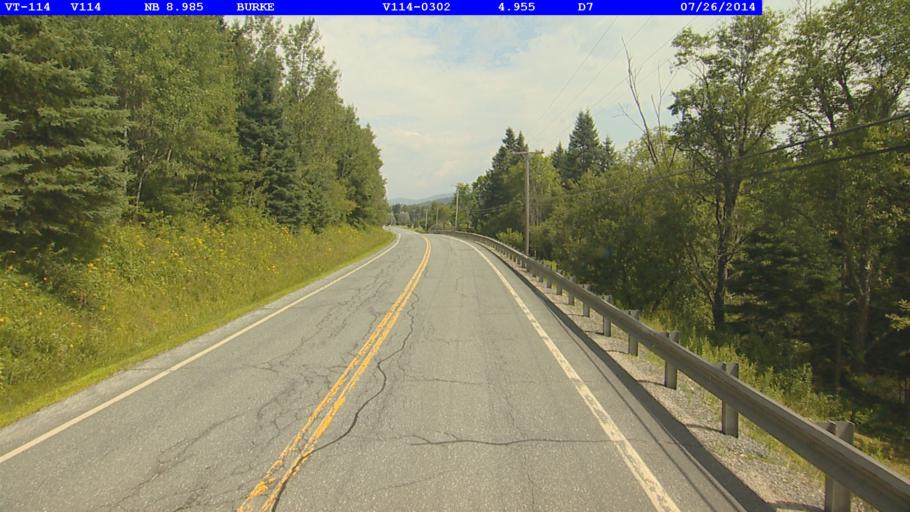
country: US
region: Vermont
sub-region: Caledonia County
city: Lyndonville
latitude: 44.6382
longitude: -71.8951
